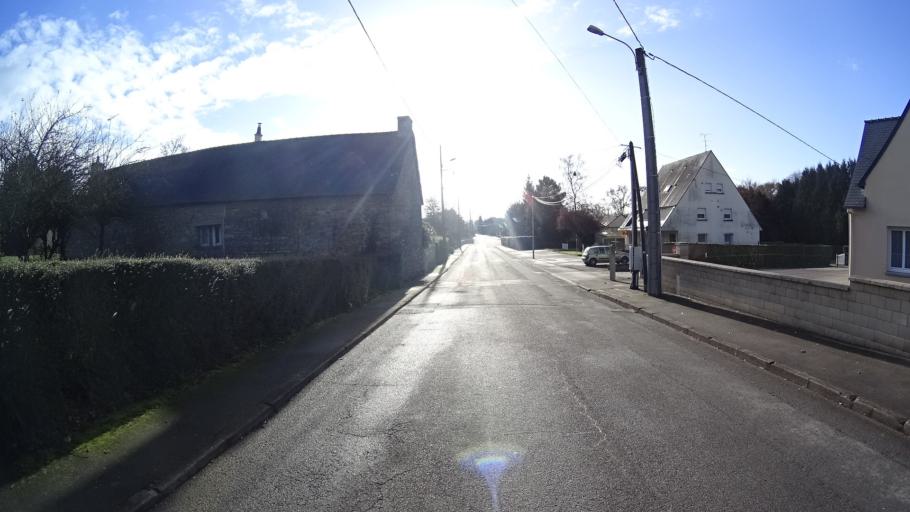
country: FR
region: Brittany
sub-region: Departement du Morbihan
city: Carentoir
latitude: 47.8159
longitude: -2.1344
